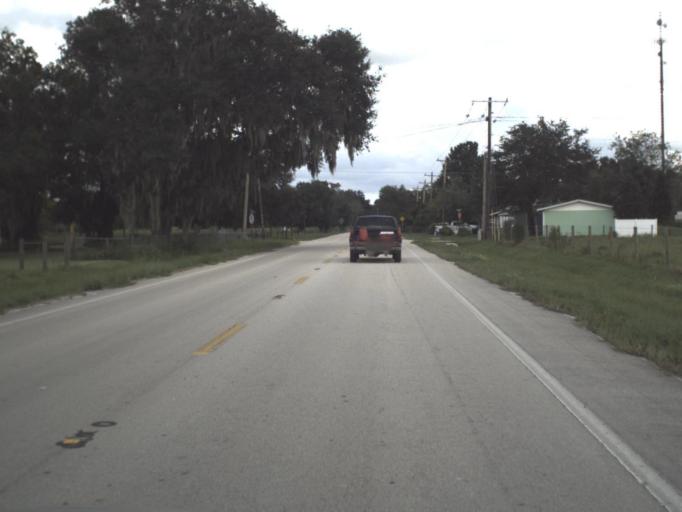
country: US
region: Florida
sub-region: Hardee County
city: Zolfo Springs
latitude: 27.5022
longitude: -81.7774
